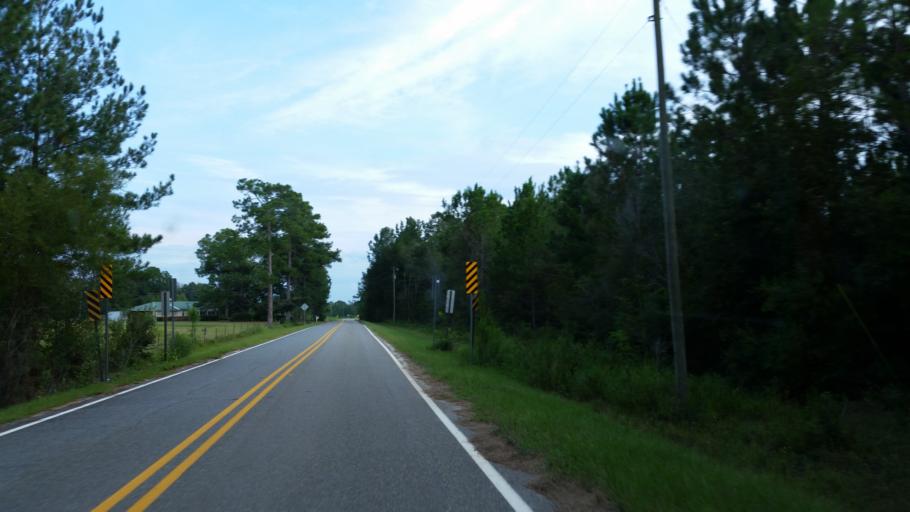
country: US
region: Georgia
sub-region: Lowndes County
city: Hahira
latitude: 31.0283
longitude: -83.3924
